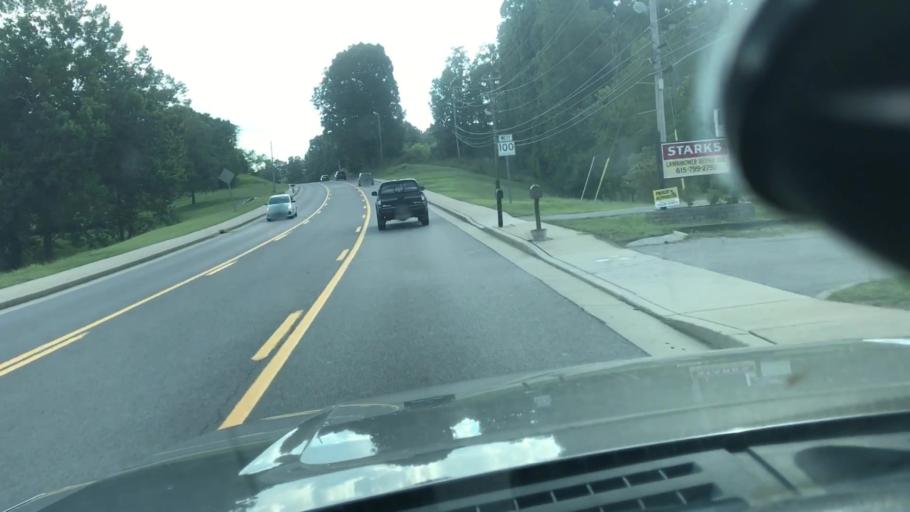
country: US
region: Tennessee
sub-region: Williamson County
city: Fairview
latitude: 35.9806
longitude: -87.1231
